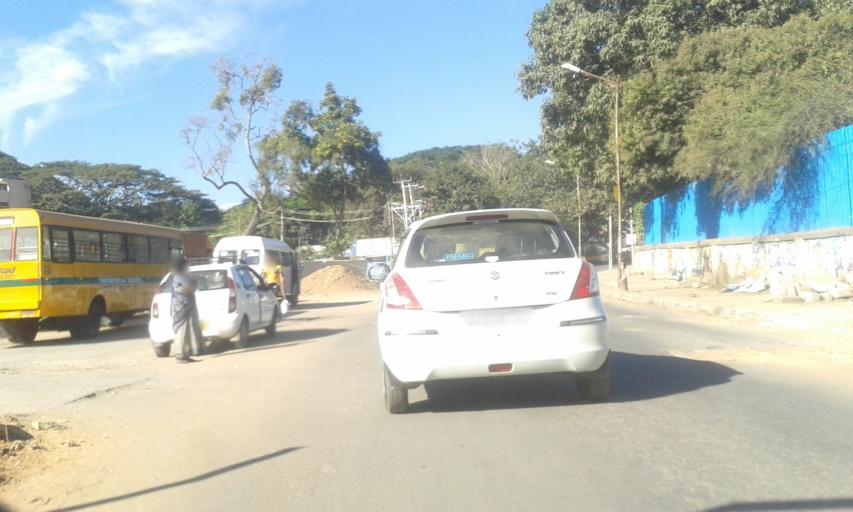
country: IN
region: Karnataka
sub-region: Bangalore Urban
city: Bangalore
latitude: 12.9616
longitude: 77.6163
